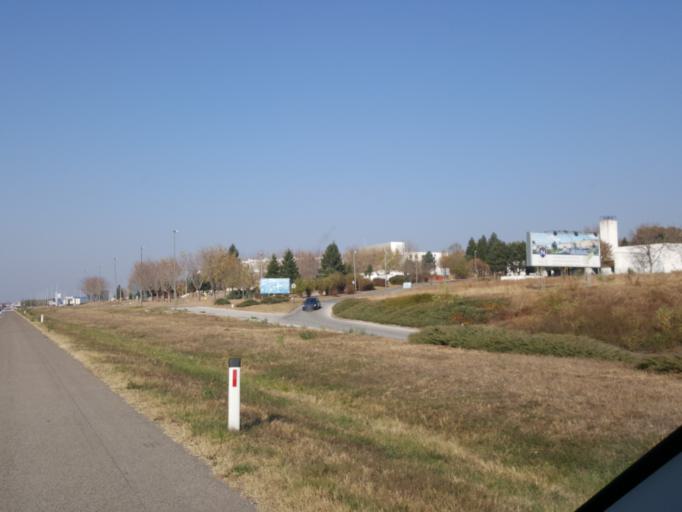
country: RS
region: Central Serbia
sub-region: Nisavski Okrug
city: Nis
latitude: 43.3810
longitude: 21.8097
